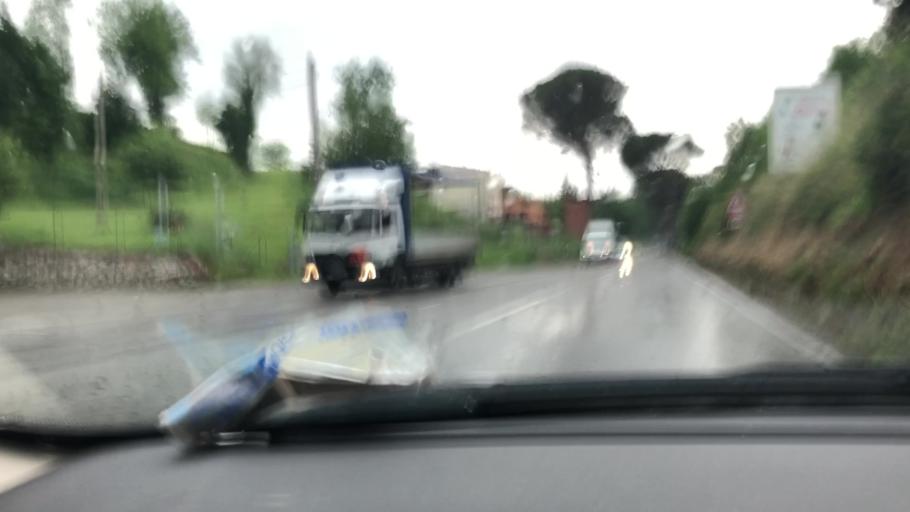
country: IT
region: Tuscany
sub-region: Province of Pisa
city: Pontedera
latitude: 43.6786
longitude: 10.6399
